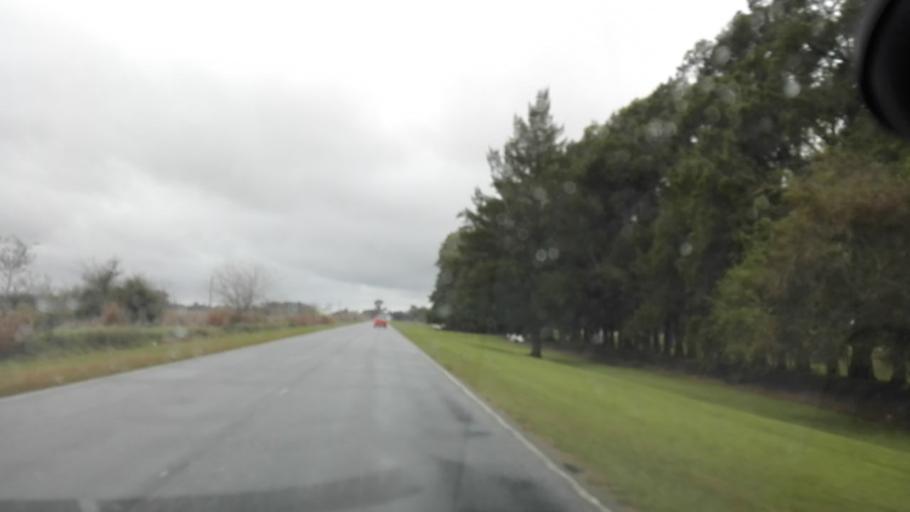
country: AR
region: Buenos Aires
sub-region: Partido de Brandsen
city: Brandsen
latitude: -35.1775
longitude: -58.2867
